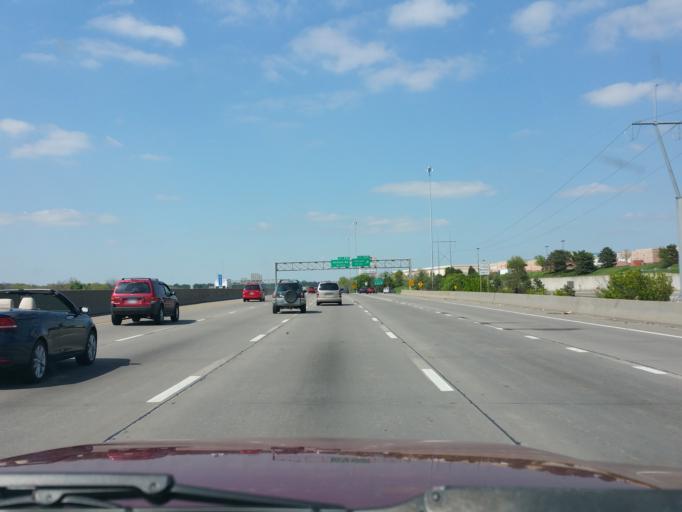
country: US
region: Kansas
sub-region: Johnson County
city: Merriam
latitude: 39.0217
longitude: -94.6920
